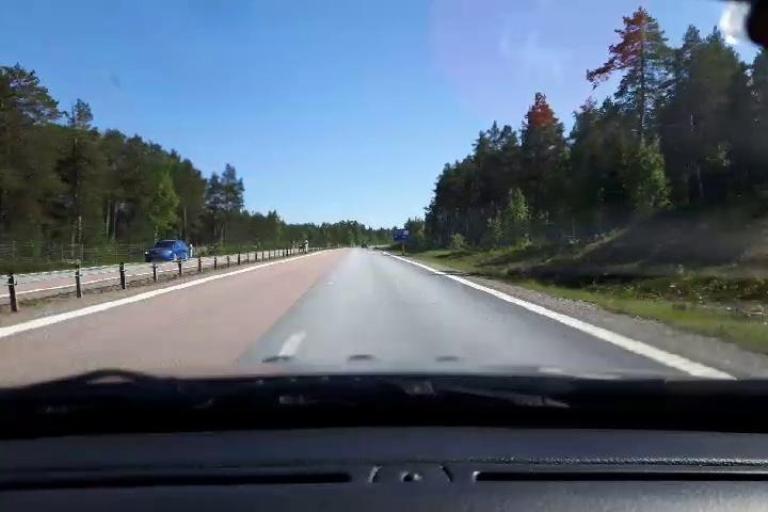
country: SE
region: Gaevleborg
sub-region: Soderhamns Kommun
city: Soderhamn
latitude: 61.3231
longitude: 17.0303
